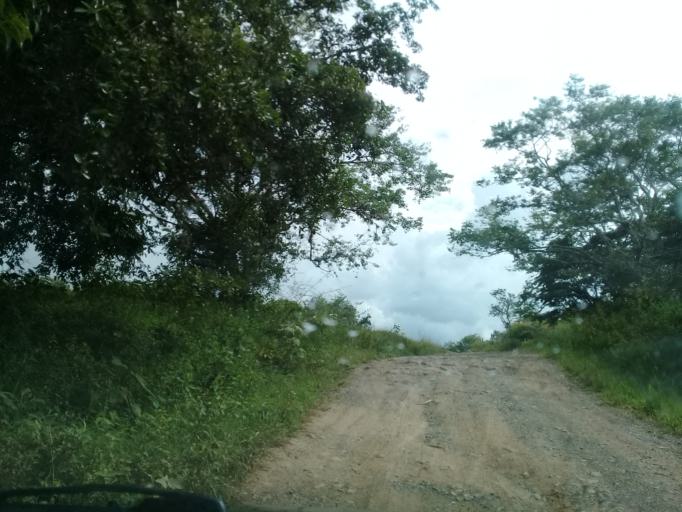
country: CO
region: Cundinamarca
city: Guaduas
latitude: 5.0882
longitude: -74.6082
